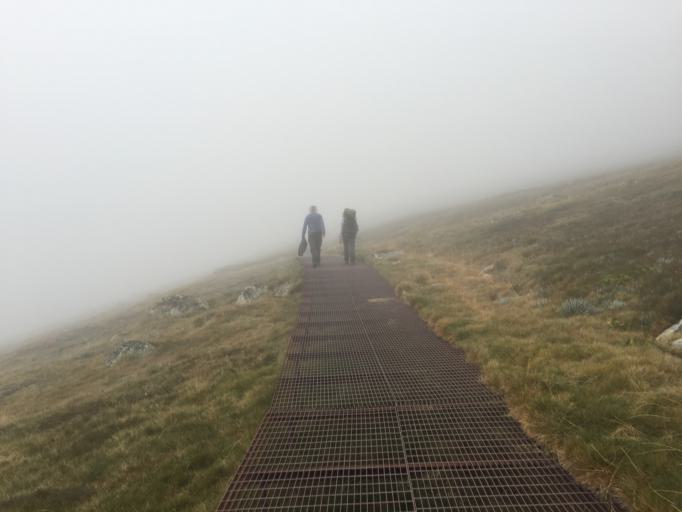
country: AU
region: New South Wales
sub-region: Snowy River
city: Jindabyne
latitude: -36.4614
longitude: 148.2703
